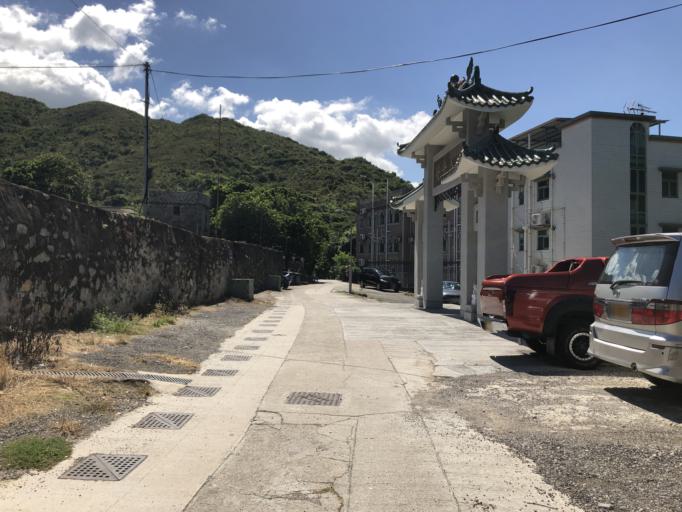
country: HK
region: Tuen Mun
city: Tuen Mun
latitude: 22.2958
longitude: 113.9715
